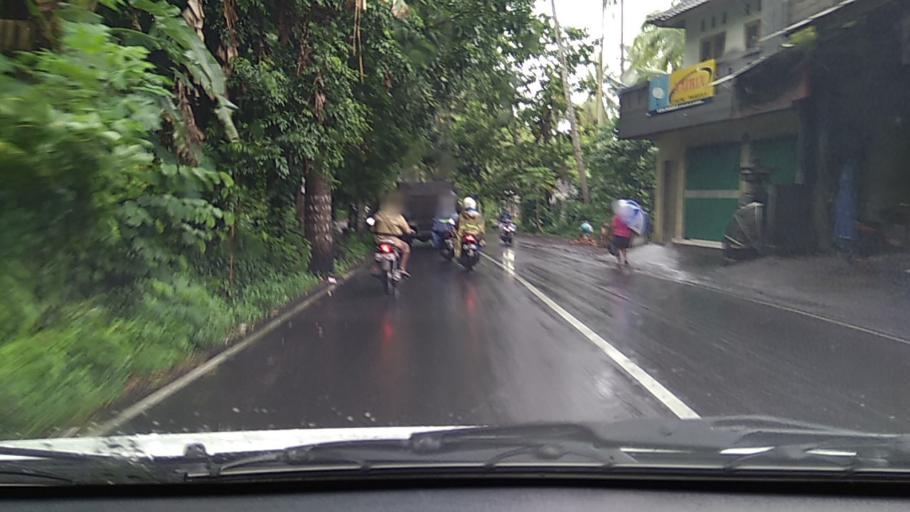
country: ID
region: Bali
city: Banjar Timbrah
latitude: -8.4801
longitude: 115.6106
